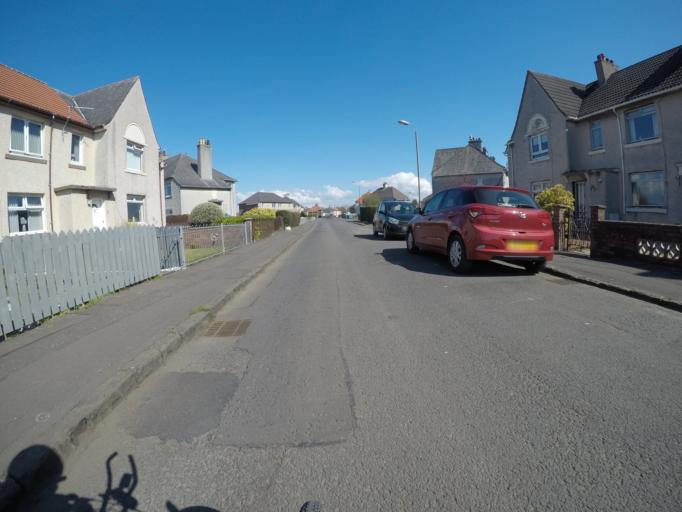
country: GB
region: Scotland
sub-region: North Ayrshire
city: Irvine
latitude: 55.6175
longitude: -4.6555
